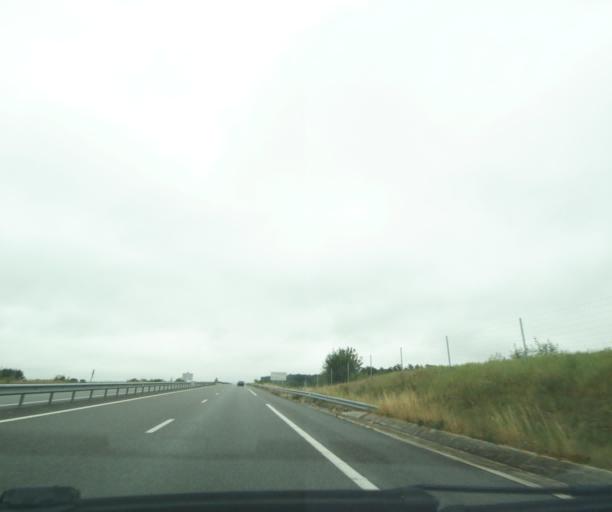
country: FR
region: Midi-Pyrenees
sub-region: Departement du Tarn
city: Le Garric
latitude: 44.0229
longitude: 2.1850
